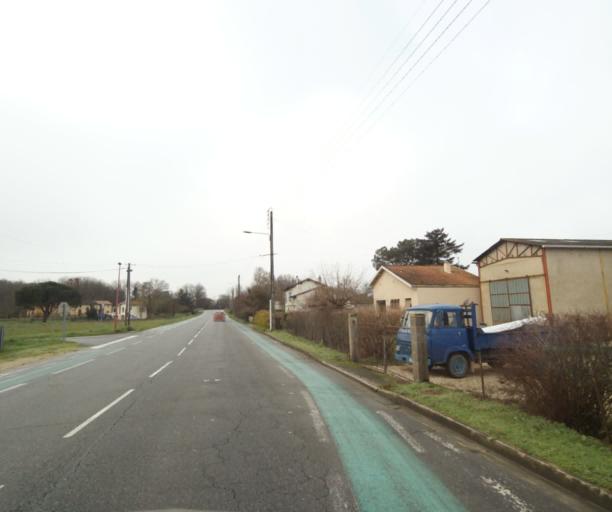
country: FR
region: Midi-Pyrenees
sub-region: Departement de la Haute-Garonne
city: Villemur-sur-Tarn
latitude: 43.8618
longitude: 1.4881
